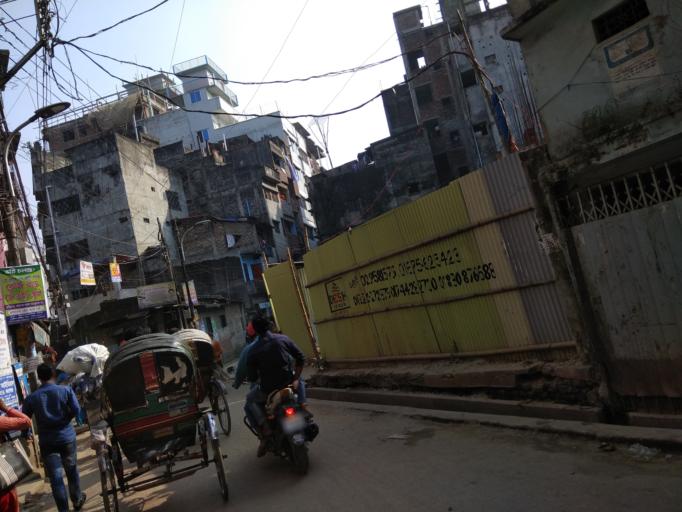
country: BD
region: Dhaka
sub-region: Dhaka
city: Dhaka
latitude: 23.7222
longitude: 90.4035
